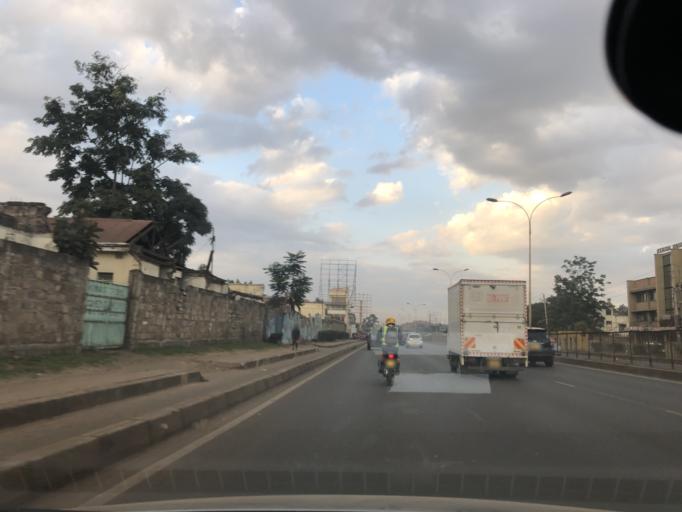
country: KE
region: Nairobi Area
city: Nairobi
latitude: -1.2714
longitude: 36.8285
